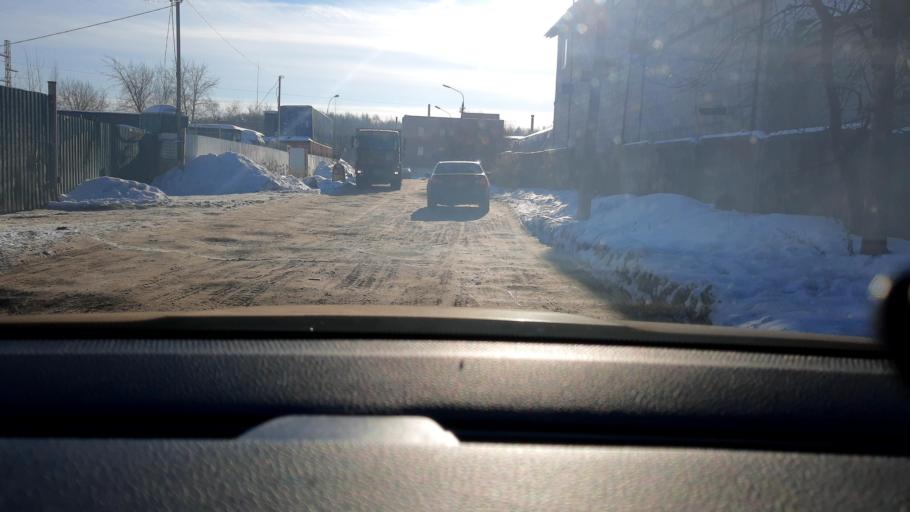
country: RU
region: Moskovskaya
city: Odintsovo
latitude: 55.6723
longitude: 37.2389
